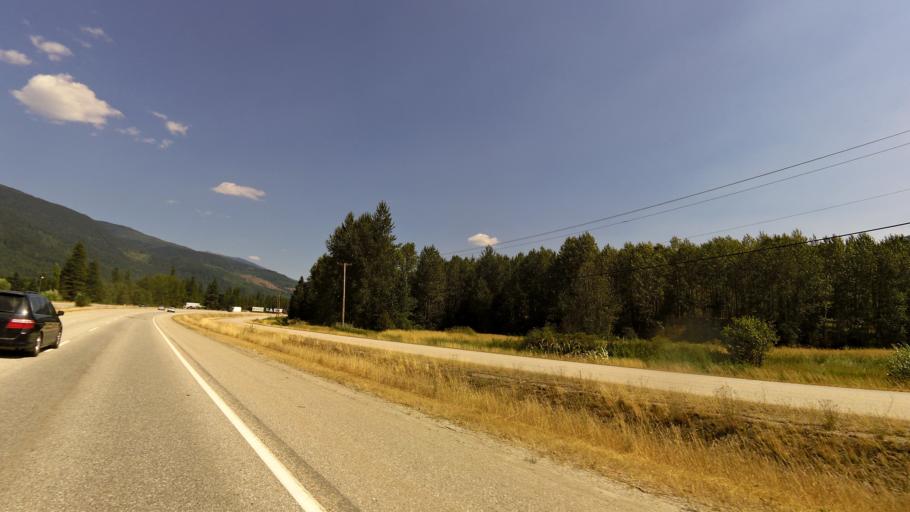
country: CA
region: British Columbia
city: Sicamous
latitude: 50.9273
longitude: -118.7941
